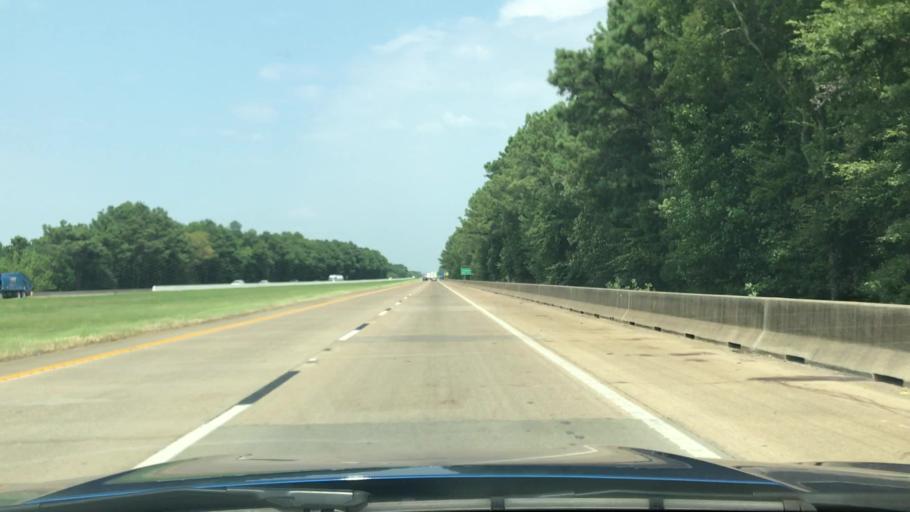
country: US
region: Texas
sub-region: Gregg County
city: Longview
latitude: 32.4350
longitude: -94.7512
